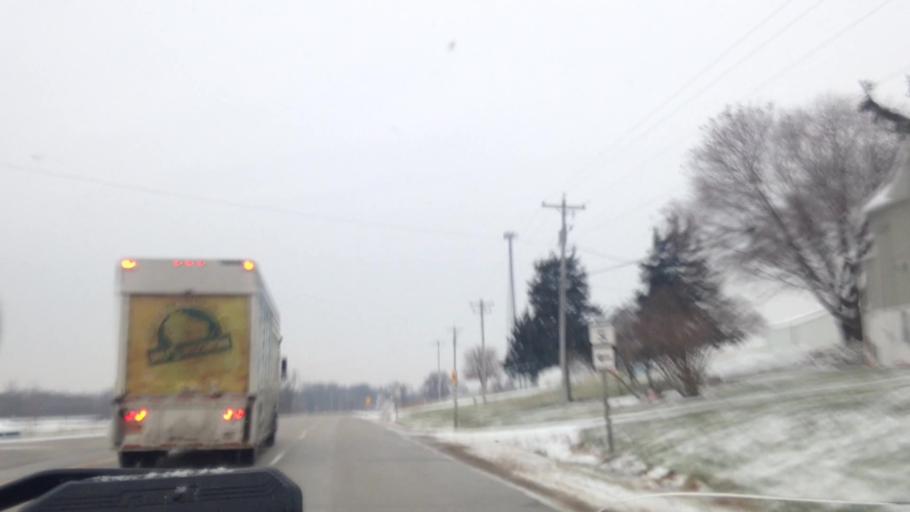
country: US
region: Wisconsin
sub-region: Dodge County
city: Hustisford
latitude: 43.3998
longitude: -88.5419
